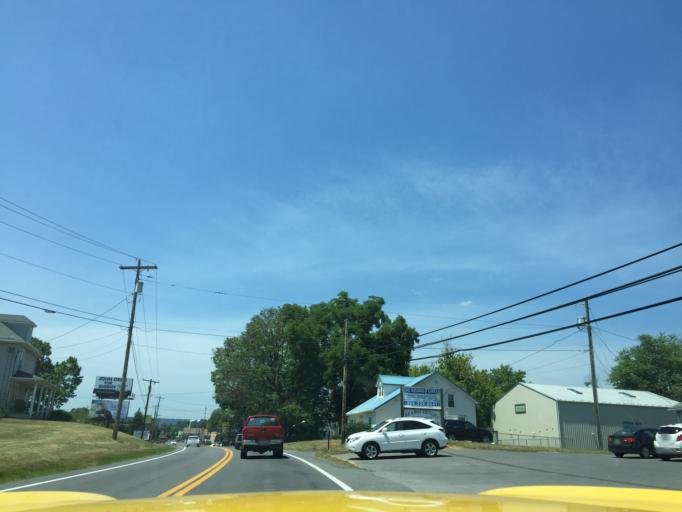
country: US
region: West Virginia
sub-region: Berkeley County
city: Inwood
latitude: 39.3564
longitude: -78.0353
